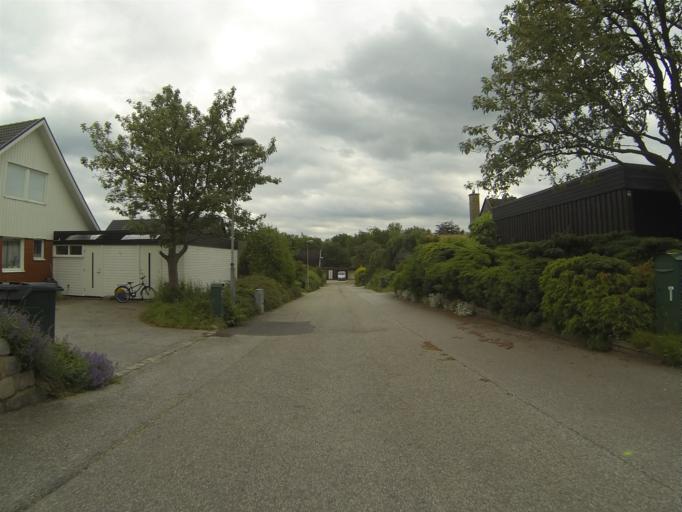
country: SE
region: Skane
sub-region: Eslovs Kommun
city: Eslov
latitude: 55.7231
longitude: 13.3355
